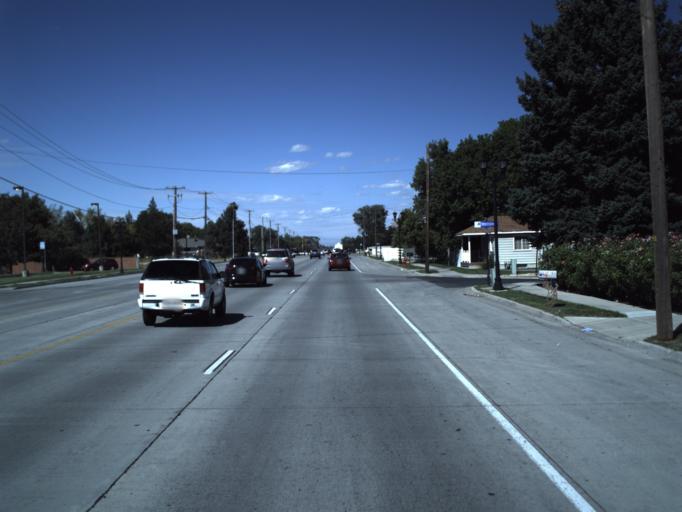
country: US
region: Utah
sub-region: Salt Lake County
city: South Jordan
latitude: 40.5672
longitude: -111.9386
